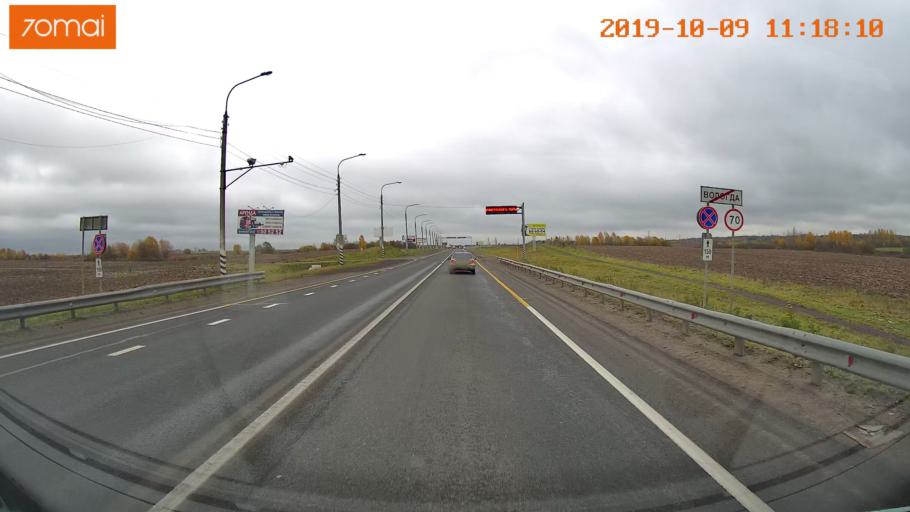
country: RU
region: Vologda
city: Vologda
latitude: 59.1699
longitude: 39.9106
